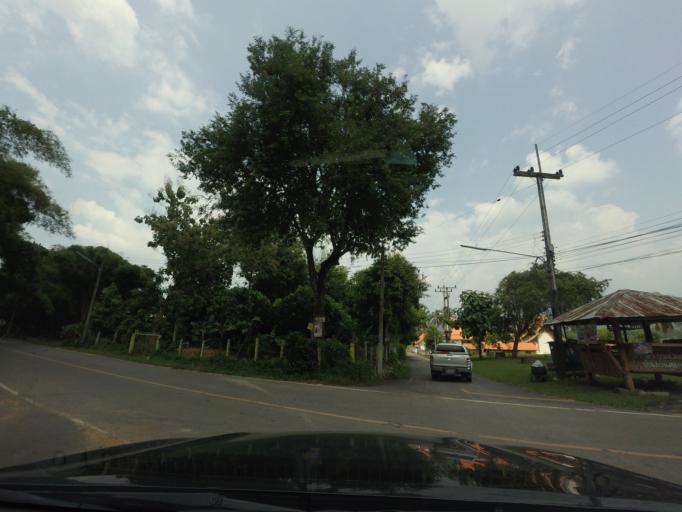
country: TH
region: Nan
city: Pua
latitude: 19.1703
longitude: 100.9271
